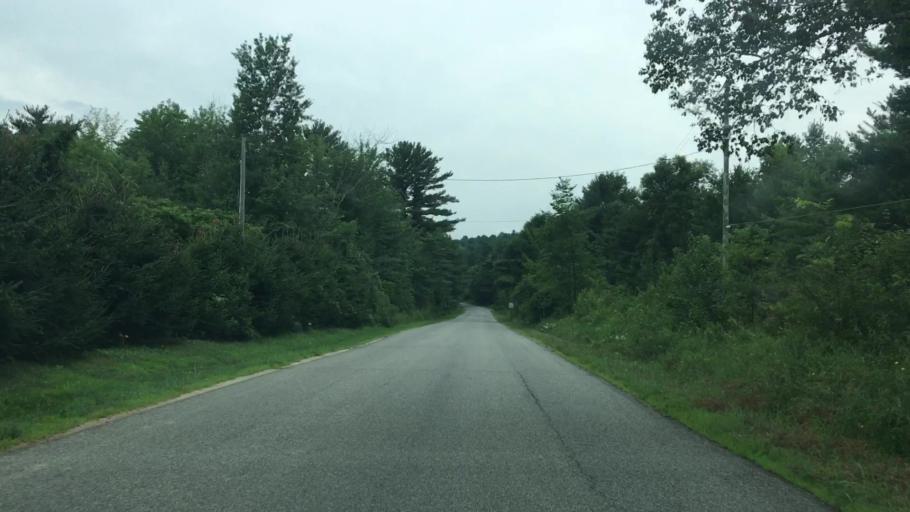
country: US
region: New York
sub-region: Essex County
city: Keeseville
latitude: 44.4555
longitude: -73.5854
